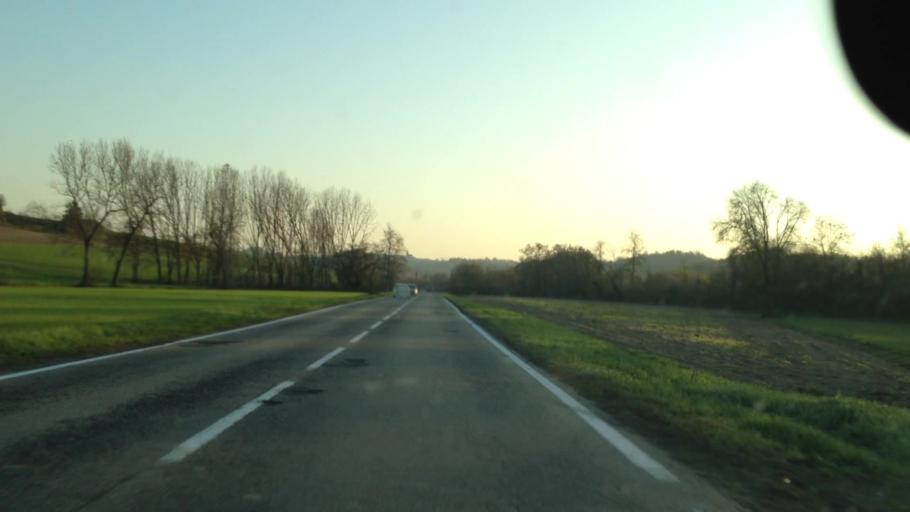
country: IT
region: Piedmont
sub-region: Provincia di Asti
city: Cunico
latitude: 45.0468
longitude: 8.1120
